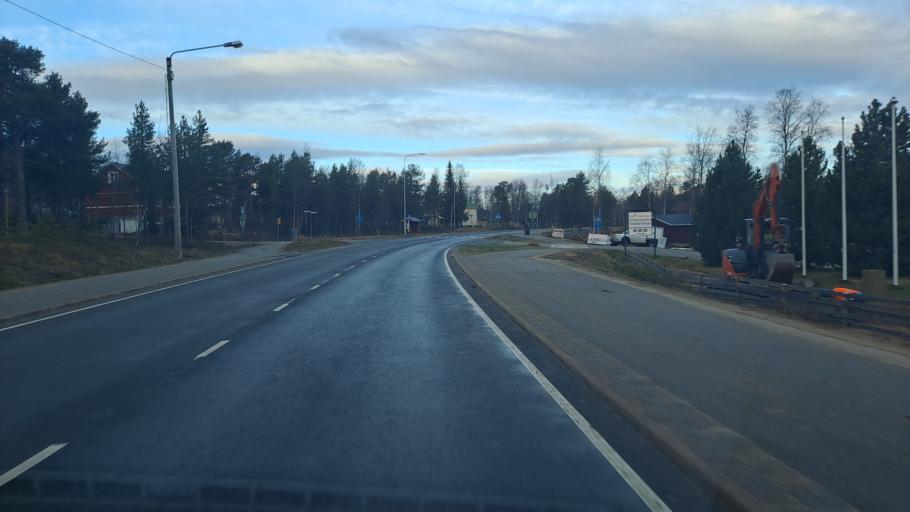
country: FI
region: Lapland
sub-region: Pohjois-Lappi
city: Inari
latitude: 68.9019
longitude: 27.0379
